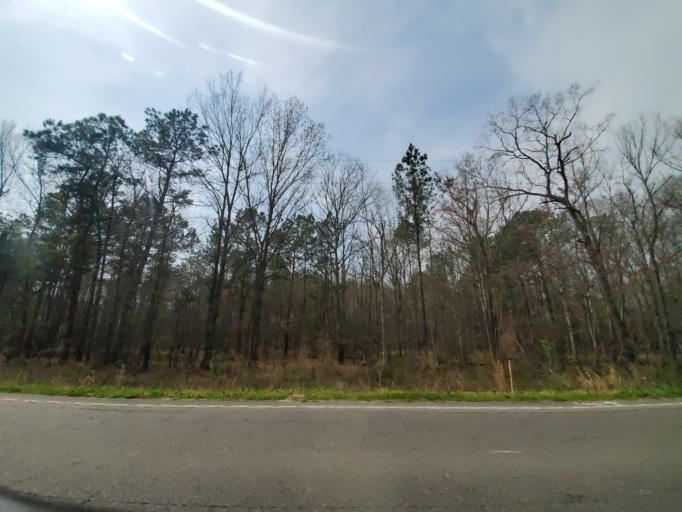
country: US
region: South Carolina
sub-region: Dorchester County
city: Ridgeville
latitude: 32.9751
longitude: -80.3066
